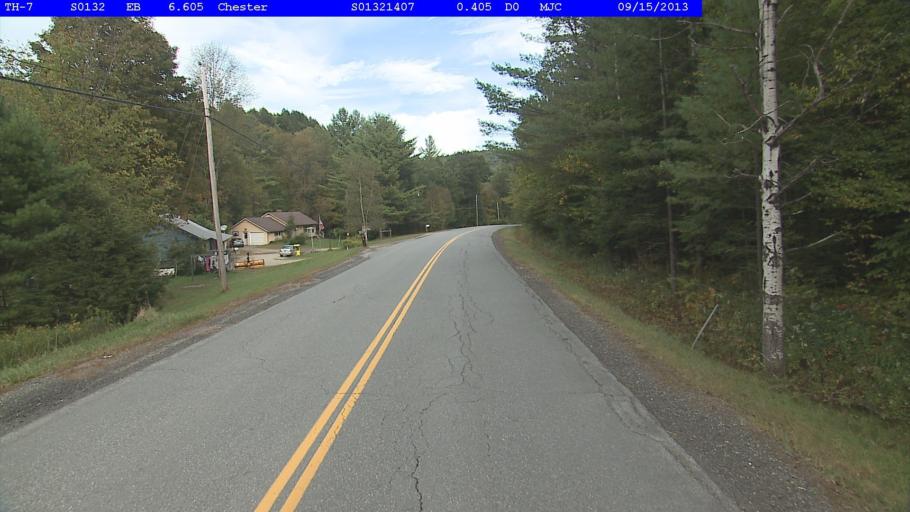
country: US
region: Vermont
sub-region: Windsor County
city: Chester
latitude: 43.2712
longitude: -72.6761
